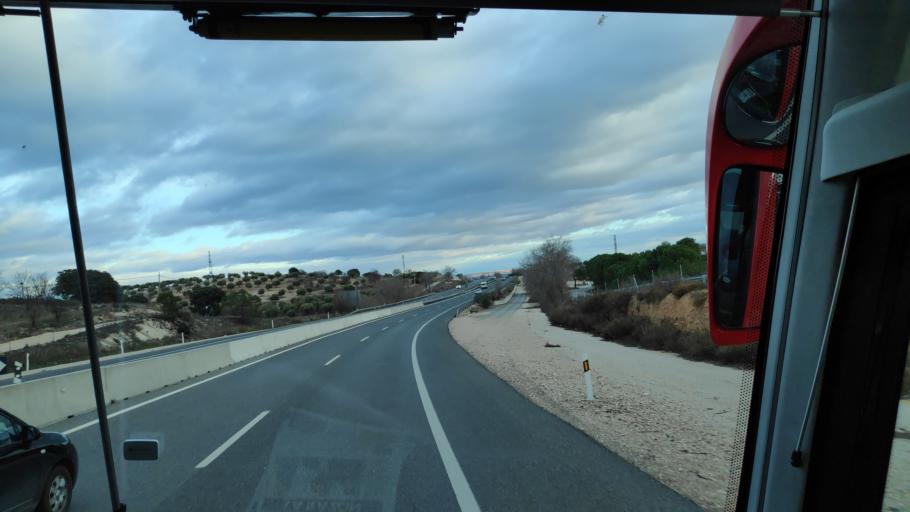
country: ES
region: Madrid
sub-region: Provincia de Madrid
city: Villarejo de Salvanes
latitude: 40.1560
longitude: -3.2541
